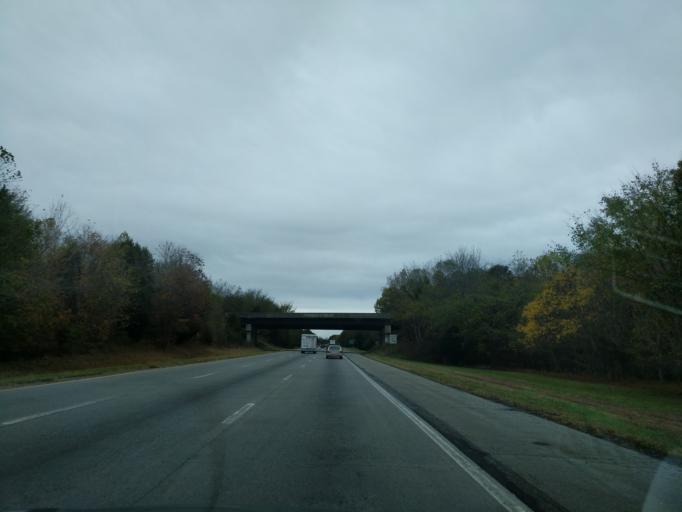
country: US
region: North Carolina
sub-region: Davidson County
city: Thomasville
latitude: 35.8488
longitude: -80.1237
